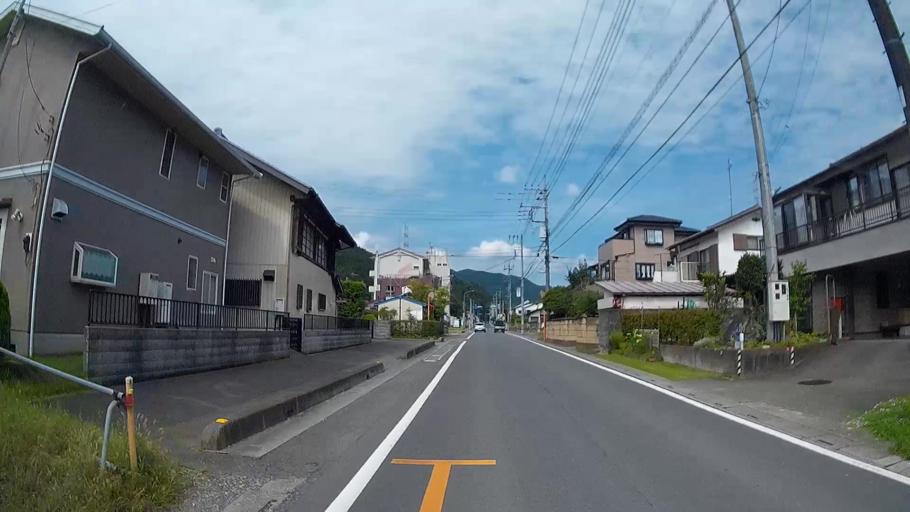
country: JP
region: Saitama
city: Hanno
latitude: 35.8680
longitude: 139.2497
